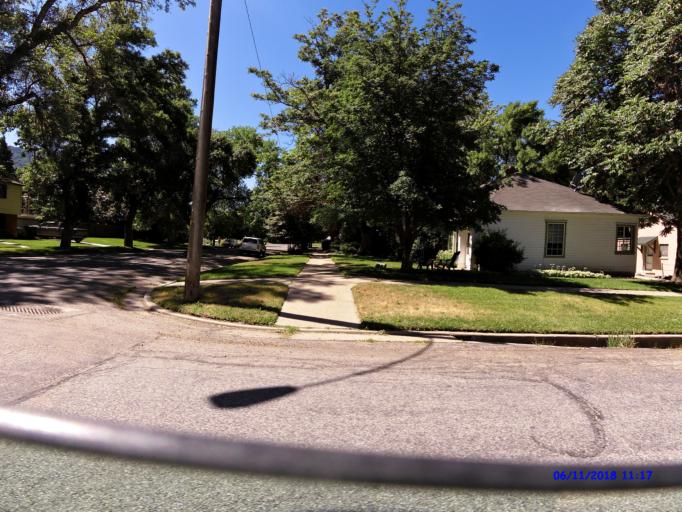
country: US
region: Utah
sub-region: Weber County
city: Ogden
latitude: 41.2213
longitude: -111.9440
